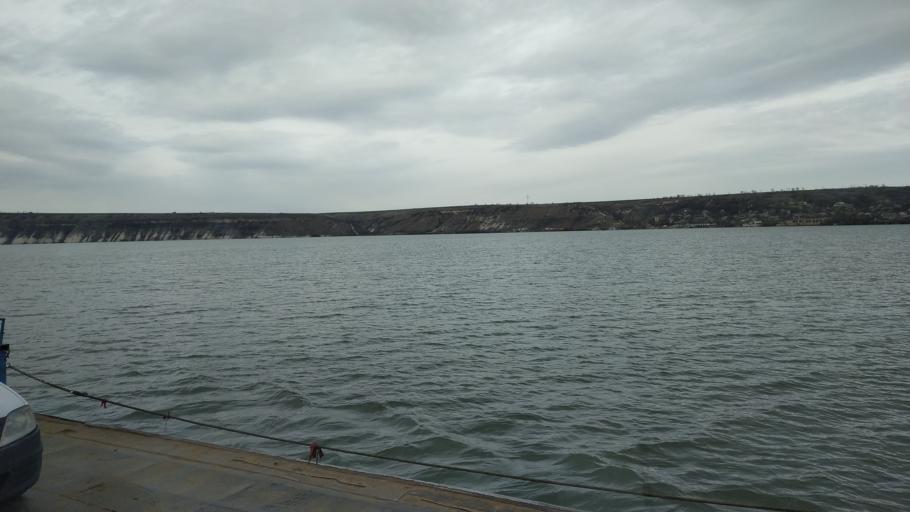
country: MD
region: Telenesti
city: Cocieri
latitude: 47.3509
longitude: 29.0997
